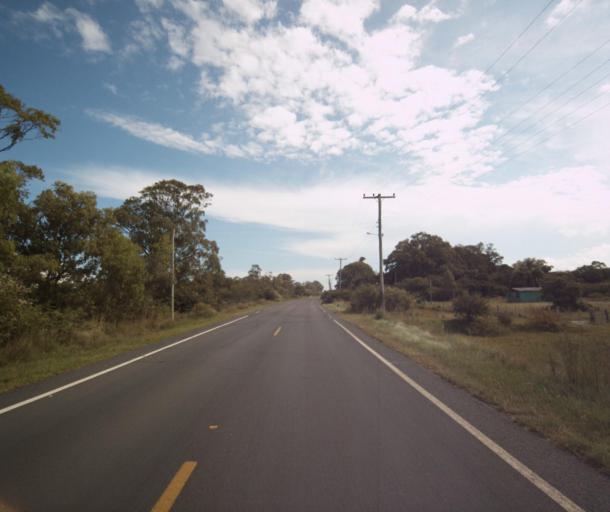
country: BR
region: Rio Grande do Sul
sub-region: Sao Lourenco Do Sul
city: Sao Lourenco do Sul
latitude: -31.6191
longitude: -51.4035
